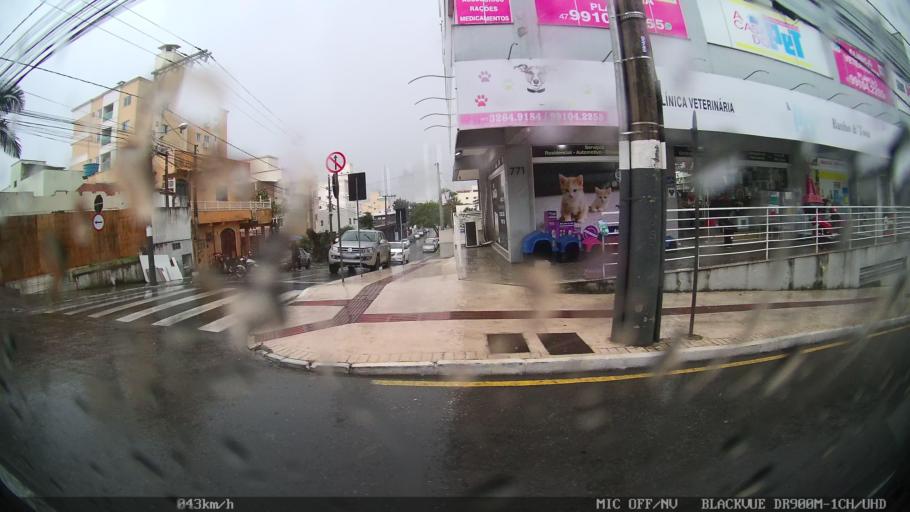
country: BR
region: Santa Catarina
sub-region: Balneario Camboriu
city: Balneario Camboriu
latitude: -26.9802
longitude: -48.6467
